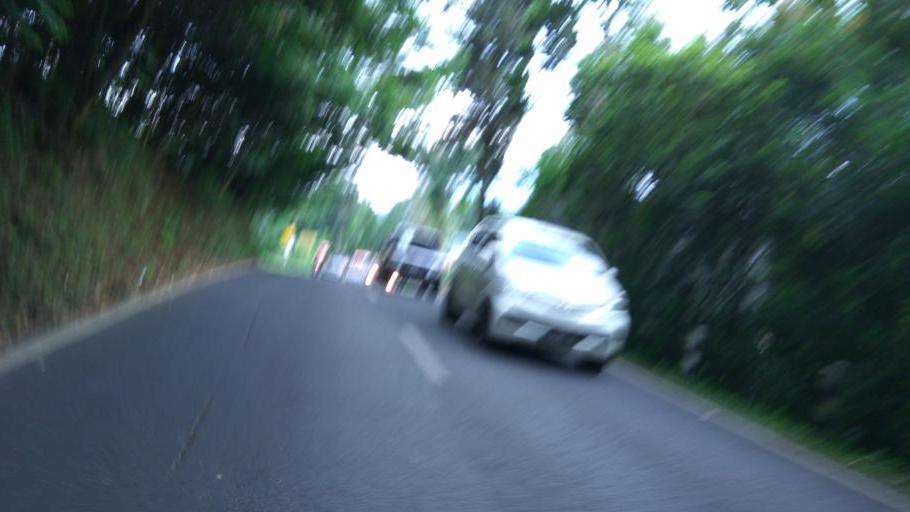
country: ID
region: Central Java
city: Gunung Kendil
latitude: -7.3771
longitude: 110.4277
